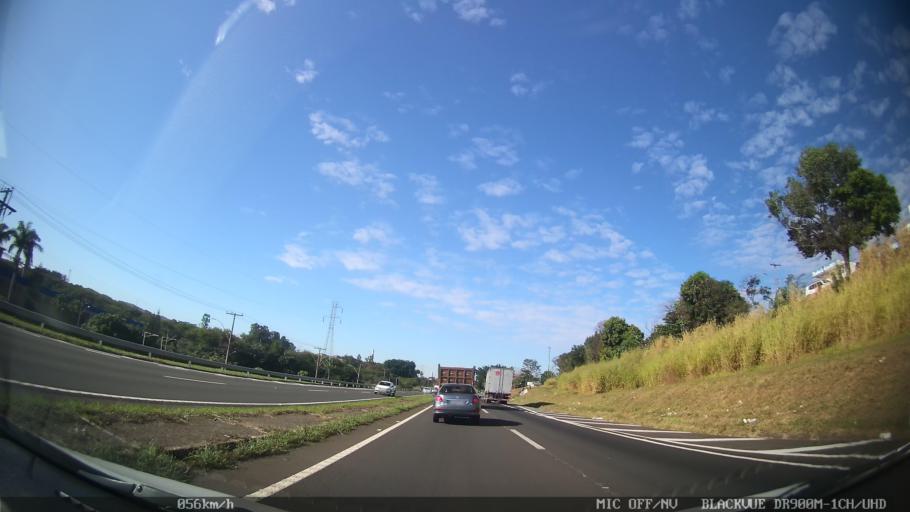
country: BR
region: Sao Paulo
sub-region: Nova Odessa
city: Nova Odessa
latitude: -22.7566
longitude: -47.3096
